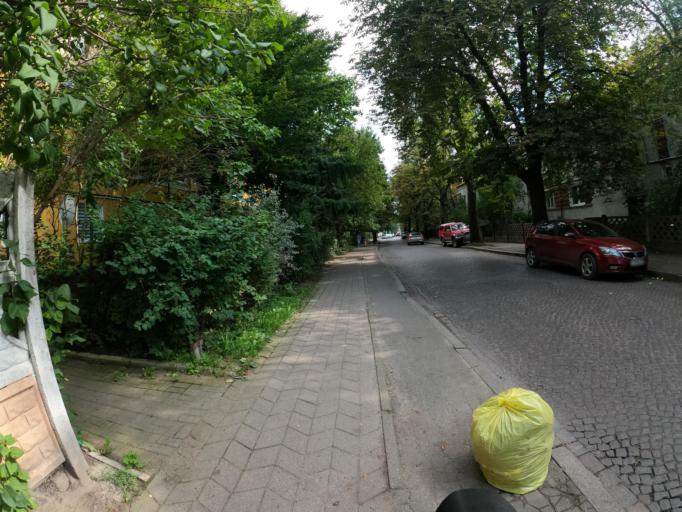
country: RU
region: Kaliningrad
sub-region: Gorod Kaliningrad
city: Kaliningrad
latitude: 54.7273
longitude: 20.4689
